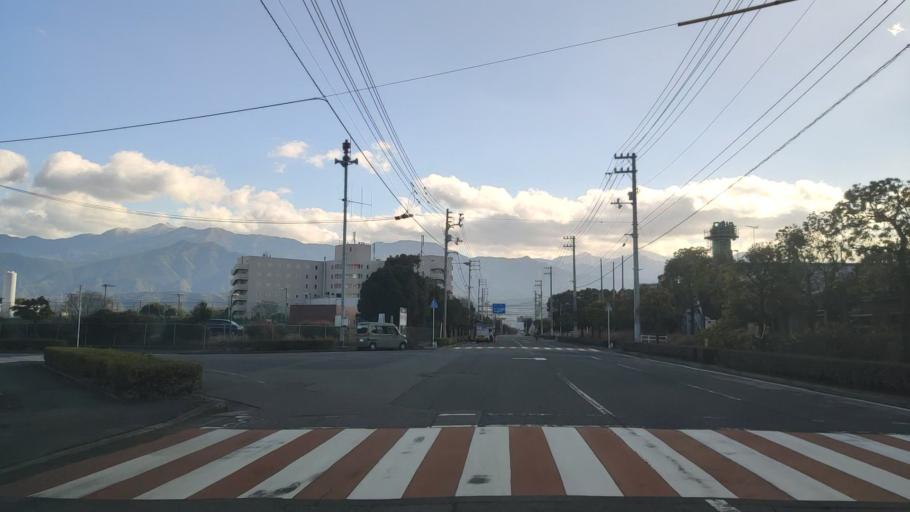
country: JP
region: Ehime
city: Saijo
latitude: 33.9372
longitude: 133.1920
